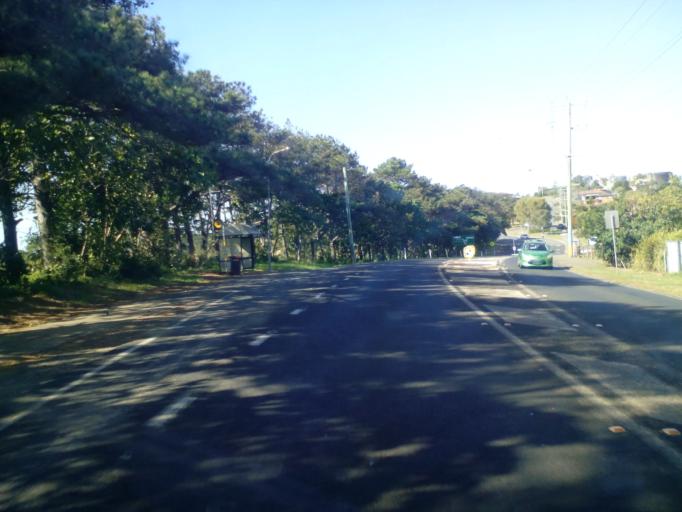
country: AU
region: New South Wales
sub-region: Tweed
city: Kingscliff
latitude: -28.2641
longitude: 153.5681
